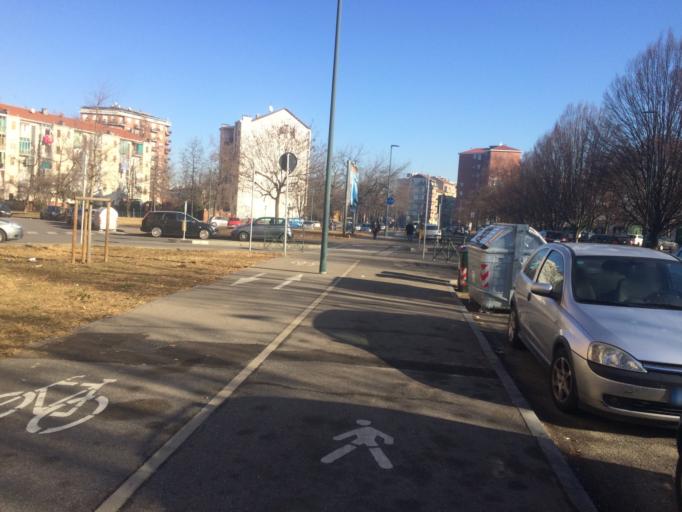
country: IT
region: Piedmont
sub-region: Provincia di Torino
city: Turin
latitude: 45.0899
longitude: 7.7033
